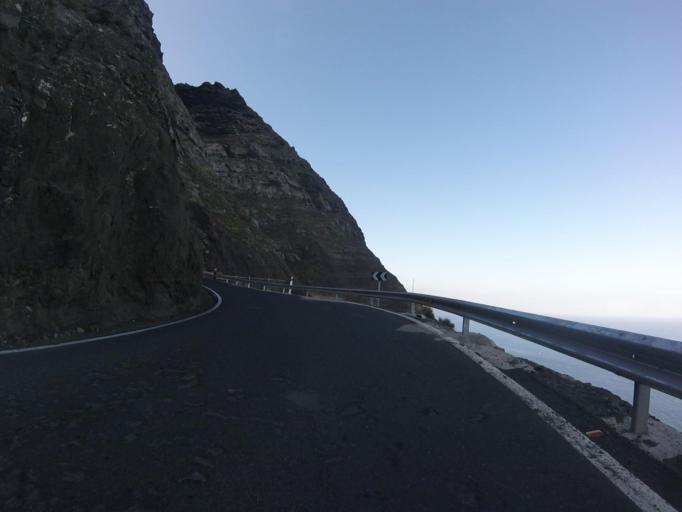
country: ES
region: Canary Islands
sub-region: Provincia de Las Palmas
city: Agaete
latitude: 28.0660
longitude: -15.7245
